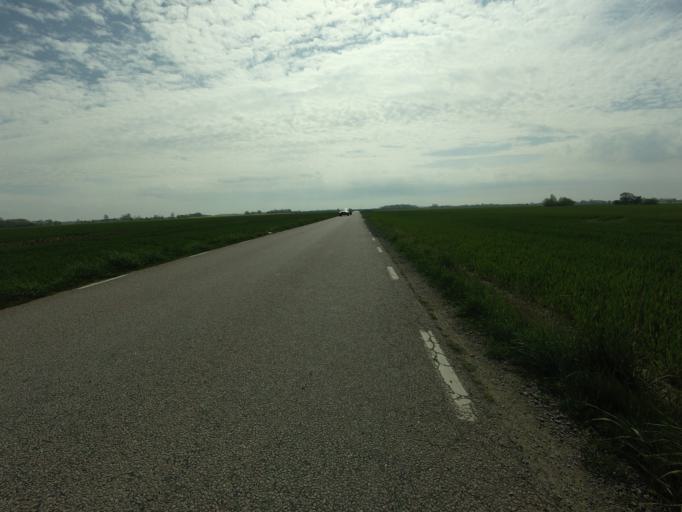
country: SE
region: Skane
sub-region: Hoganas Kommun
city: Hoganas
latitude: 56.2418
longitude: 12.5779
